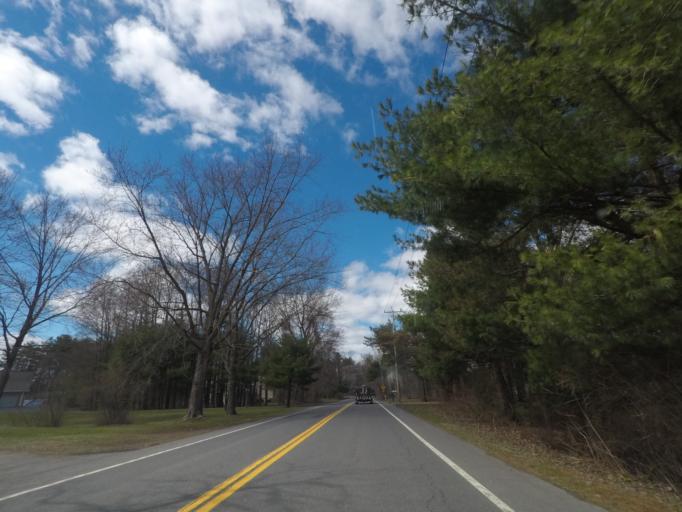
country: US
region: New York
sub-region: Albany County
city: Delmar
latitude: 42.5990
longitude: -73.8353
